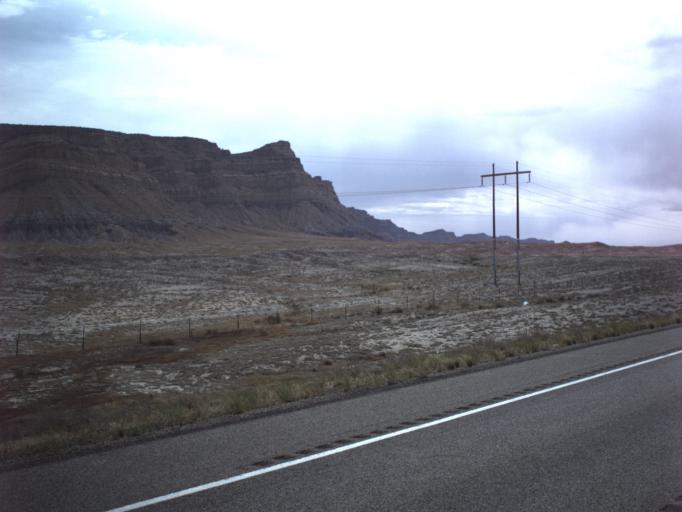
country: US
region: Utah
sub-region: Carbon County
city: East Carbon City
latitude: 39.2166
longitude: -110.3387
